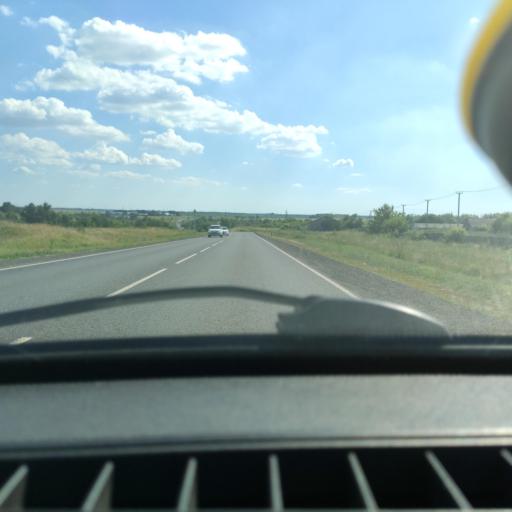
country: RU
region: Samara
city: Povolzhskiy
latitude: 53.7154
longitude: 49.7488
